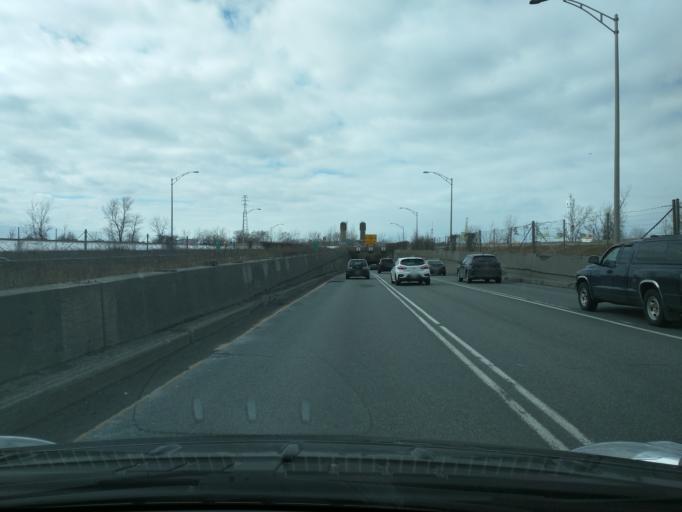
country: CA
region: Quebec
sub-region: Monteregie
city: Boucherville
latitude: 45.5813
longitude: -73.4884
